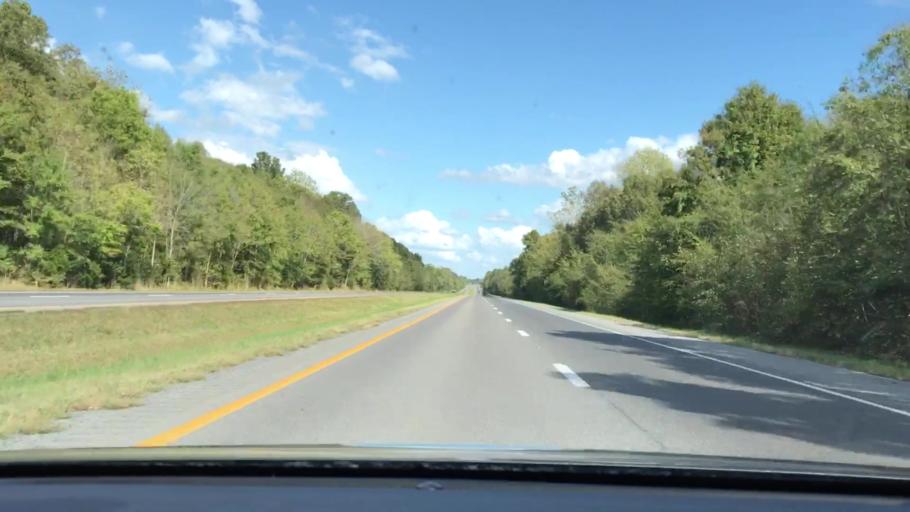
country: US
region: Kentucky
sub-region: Marshall County
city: Benton
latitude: 36.8300
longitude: -88.4499
